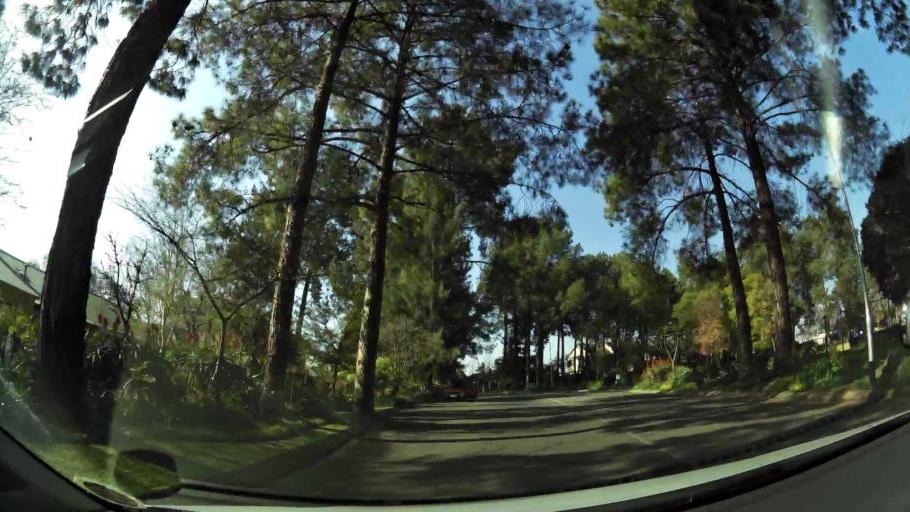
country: ZA
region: Gauteng
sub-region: City of Johannesburg Metropolitan Municipality
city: Modderfontein
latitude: -26.1042
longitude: 28.1539
